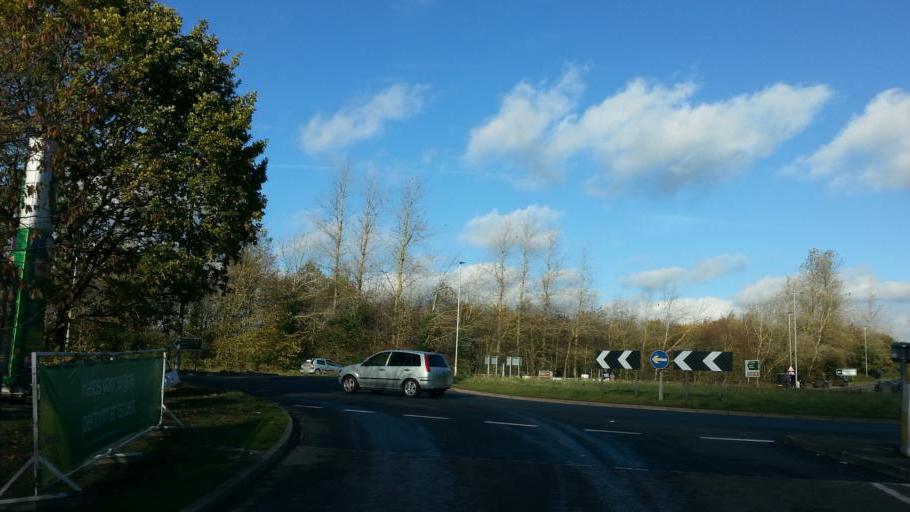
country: GB
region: England
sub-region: Suffolk
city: Beccles
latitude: 52.4750
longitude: 1.5462
